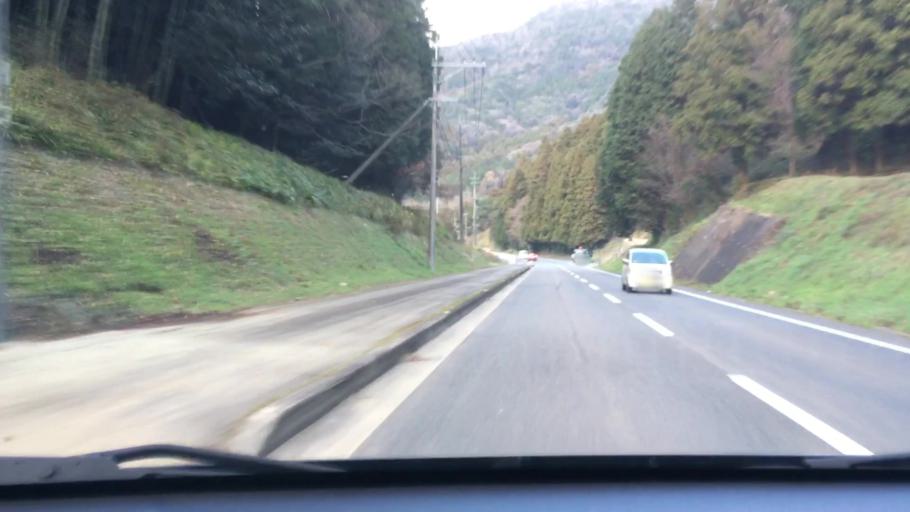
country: JP
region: Oita
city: Bungo-Takada-shi
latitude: 33.4773
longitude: 131.3854
